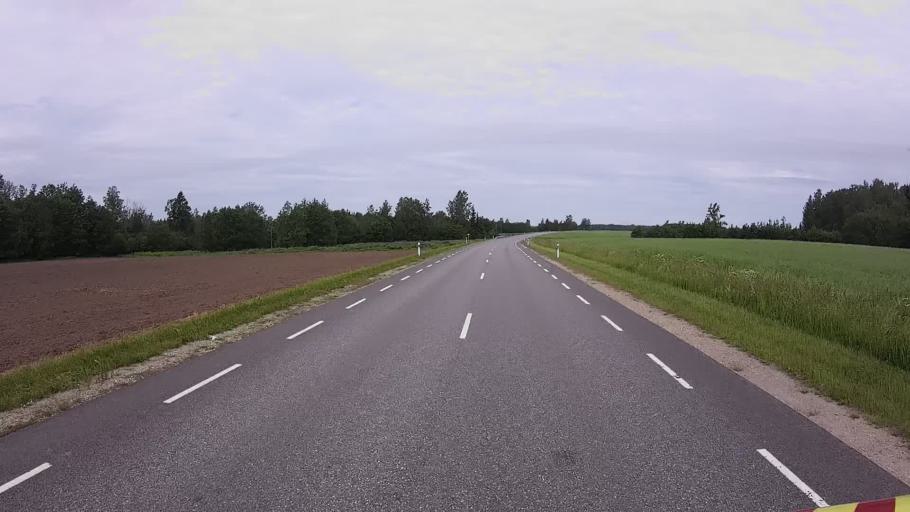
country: EE
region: Viljandimaa
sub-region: Karksi vald
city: Karksi-Nuia
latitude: 58.1596
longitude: 25.5913
